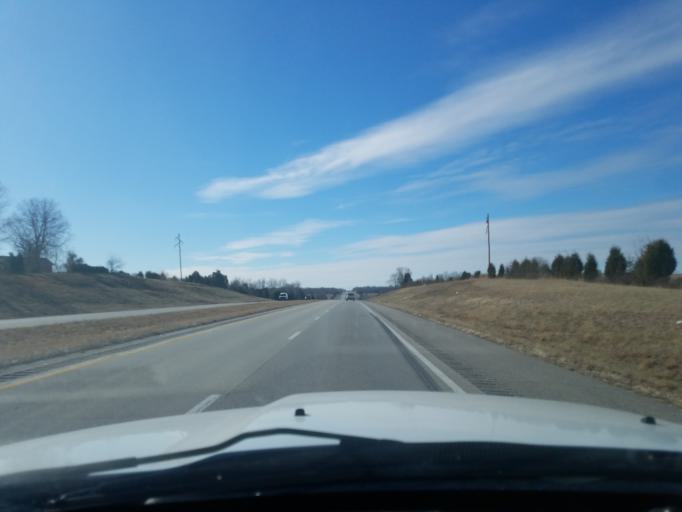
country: US
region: Kentucky
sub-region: Grayson County
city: Leitchfield
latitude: 37.4843
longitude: -86.2221
